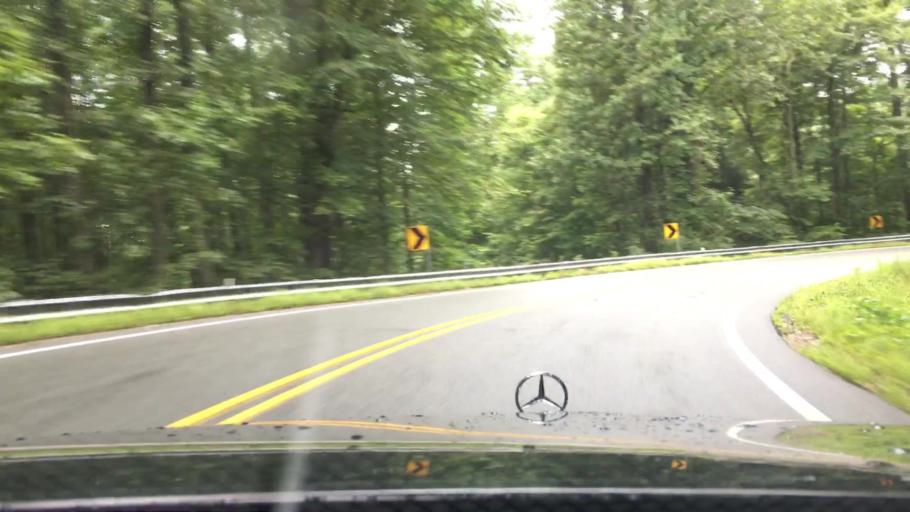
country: US
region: Virginia
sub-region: Nelson County
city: Nellysford
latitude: 37.8511
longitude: -78.9230
